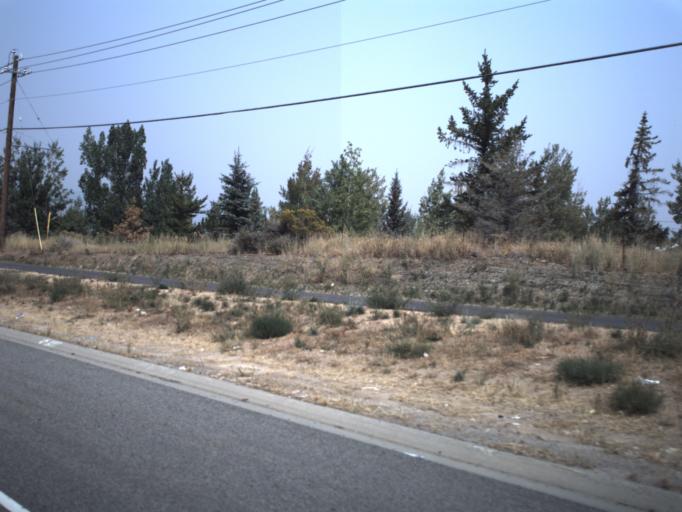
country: US
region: Utah
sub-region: Summit County
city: Snyderville
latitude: 40.6989
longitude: -111.5442
